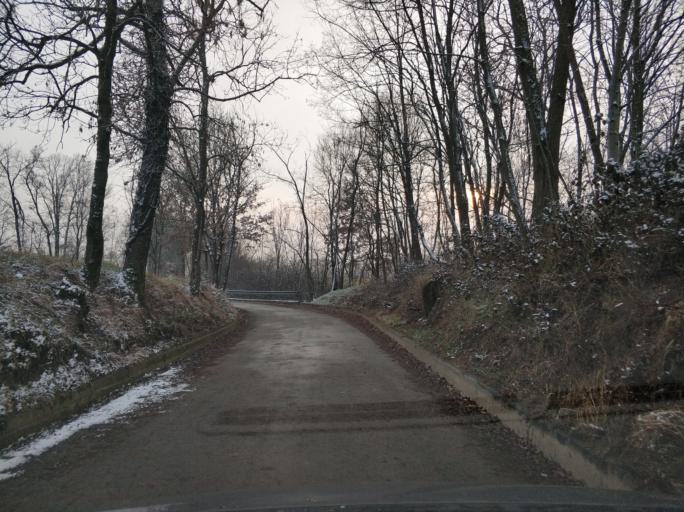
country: IT
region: Piedmont
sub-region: Provincia di Torino
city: San Francesco al Campo
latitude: 45.2222
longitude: 7.6703
